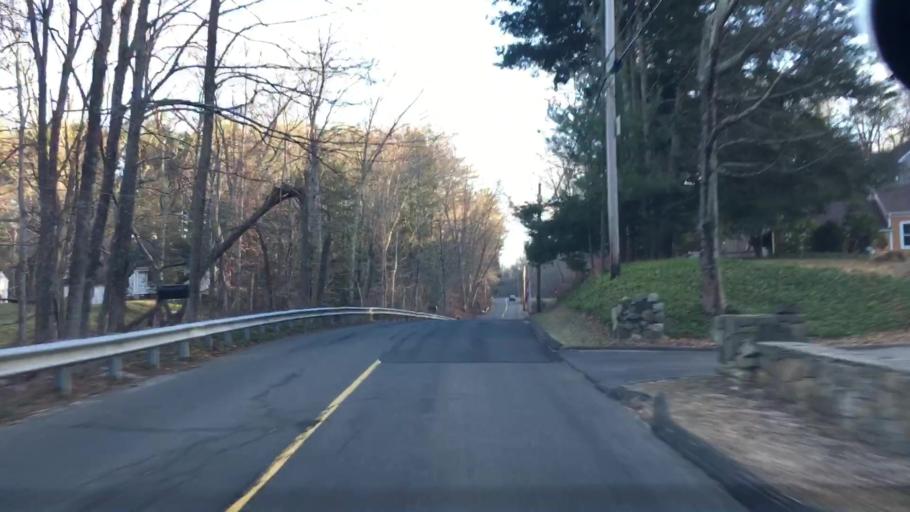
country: US
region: Connecticut
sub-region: Fairfield County
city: Newtown
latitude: 41.4513
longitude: -73.3231
